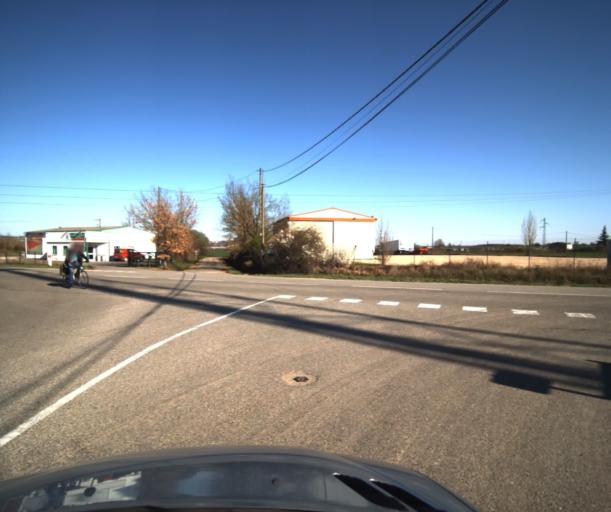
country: FR
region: Midi-Pyrenees
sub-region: Departement du Tarn-et-Garonne
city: Bressols
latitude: 43.9463
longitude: 1.3274
